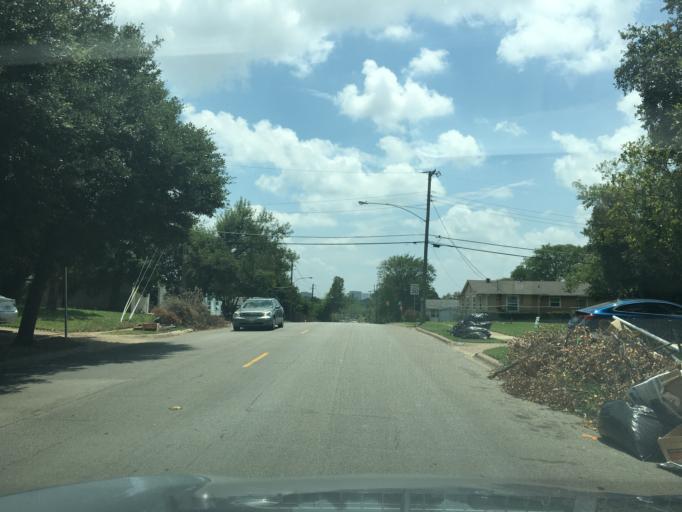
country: US
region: Texas
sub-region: Dallas County
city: Richardson
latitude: 32.9128
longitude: -96.7627
